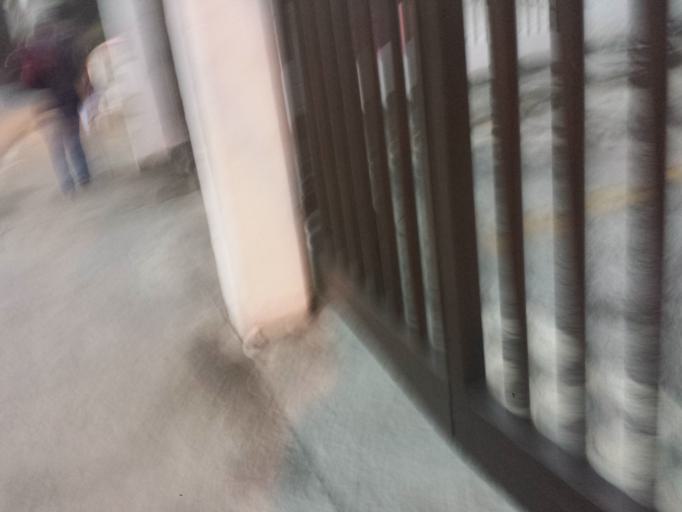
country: CO
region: Antioquia
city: Itagui
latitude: 6.1970
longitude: -75.5802
